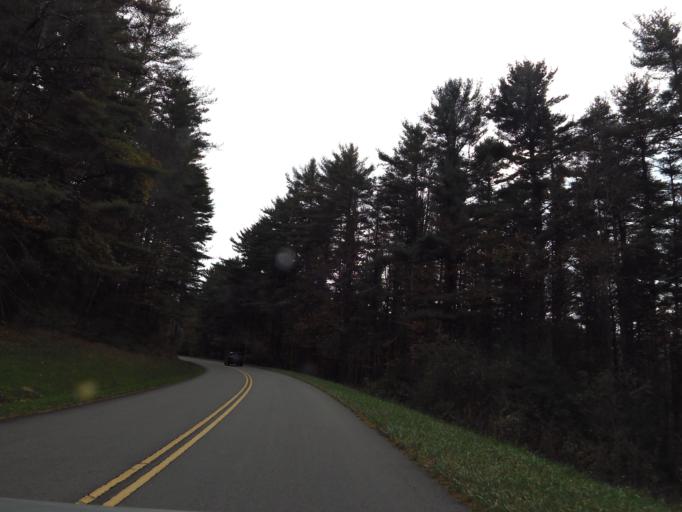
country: US
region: North Carolina
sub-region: Wilkes County
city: Mulberry
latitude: 36.3733
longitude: -81.2910
